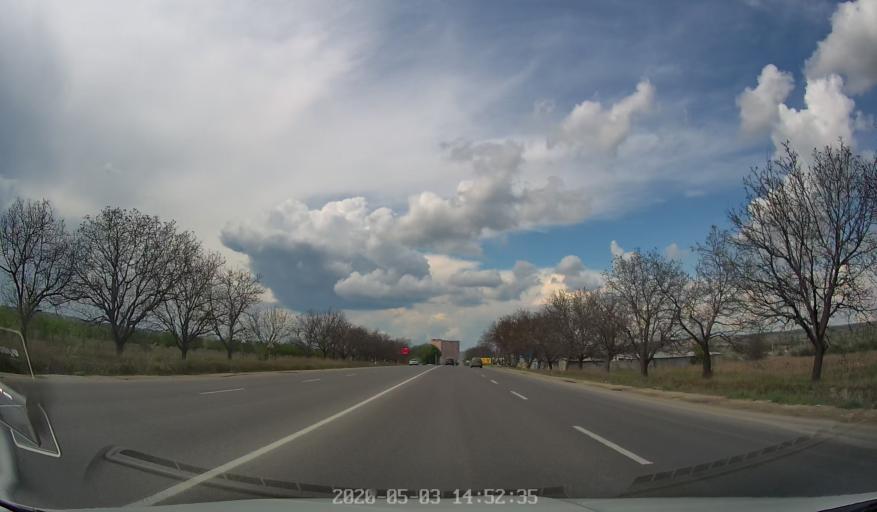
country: MD
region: Chisinau
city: Vatra
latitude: 47.0655
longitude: 28.7426
